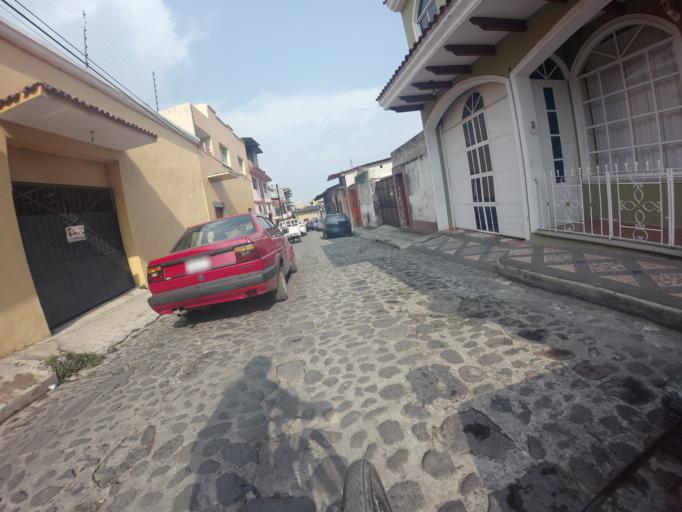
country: MX
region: Veracruz
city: Xico
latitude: 19.4218
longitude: -97.0095
